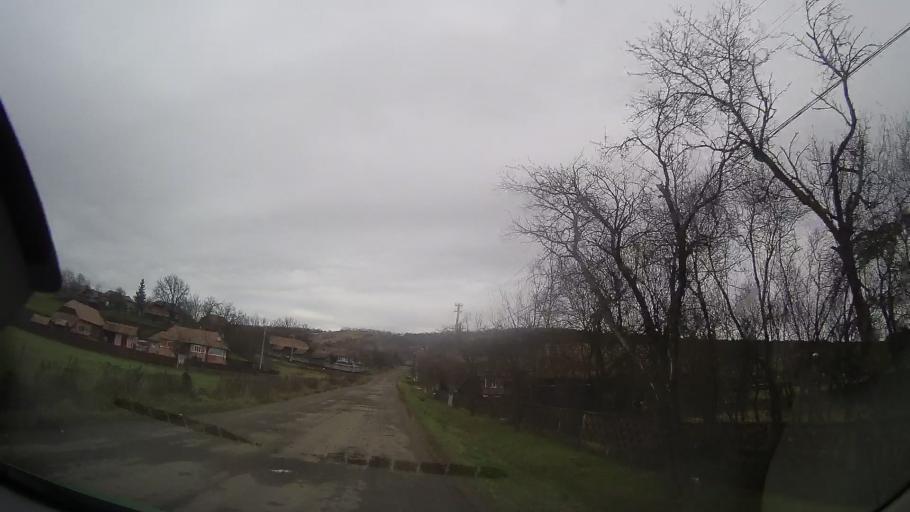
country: RO
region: Mures
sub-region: Comuna Bala
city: Bala
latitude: 46.7089
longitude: 24.5013
